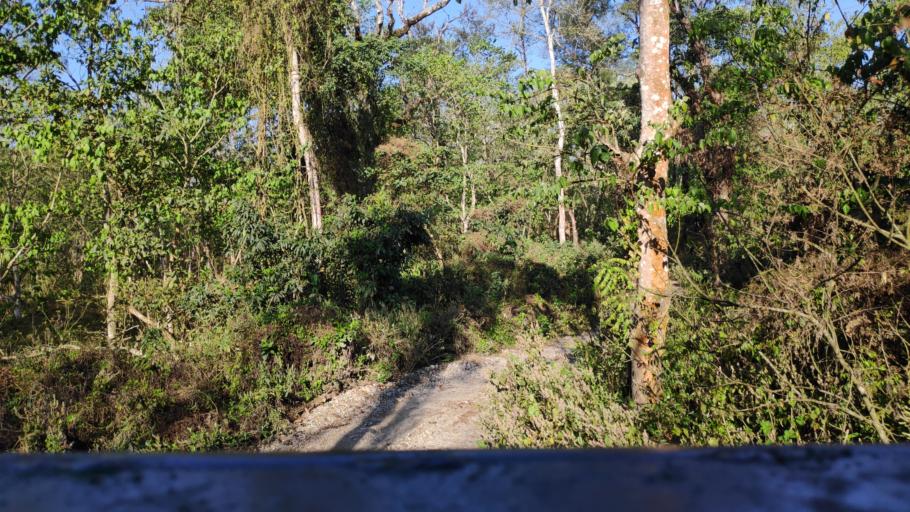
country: NP
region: Central Region
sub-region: Narayani Zone
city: Bharatpur
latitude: 27.5597
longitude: 84.5408
